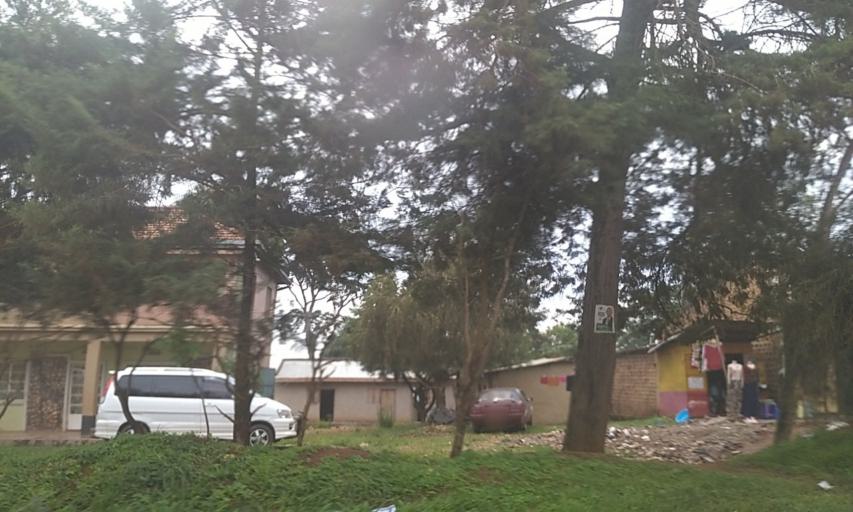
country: UG
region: Central Region
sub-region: Wakiso District
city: Bweyogerere
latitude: 0.3944
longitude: 32.6642
